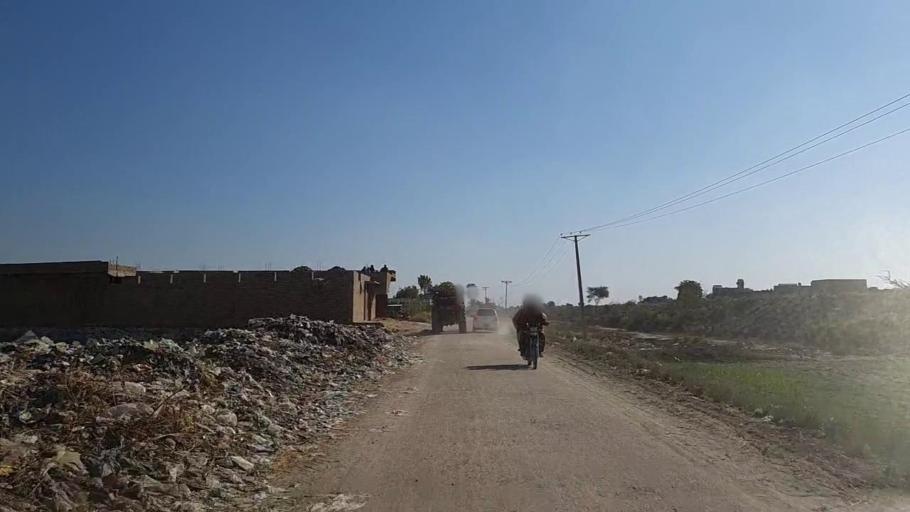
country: PK
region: Sindh
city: Nawabshah
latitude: 26.2405
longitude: 68.4238
